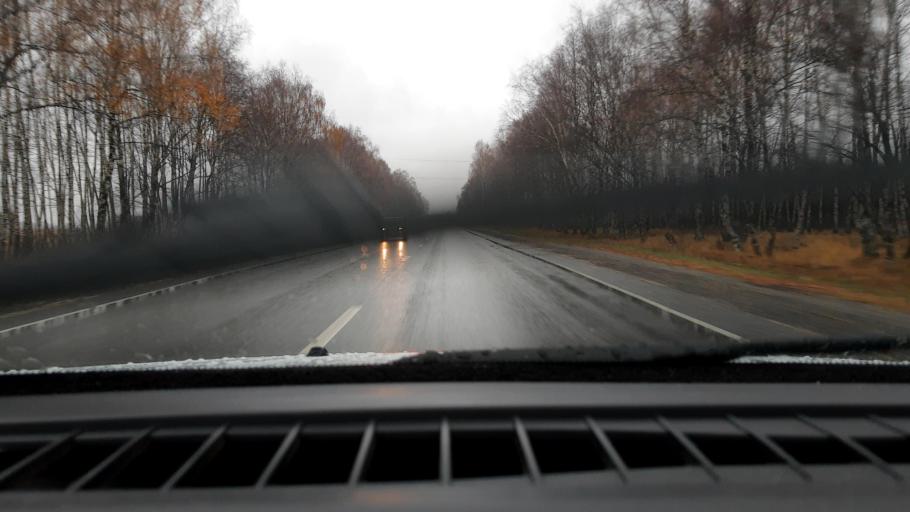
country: RU
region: Nizjnij Novgorod
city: Sitniki
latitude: 56.5186
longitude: 44.0253
